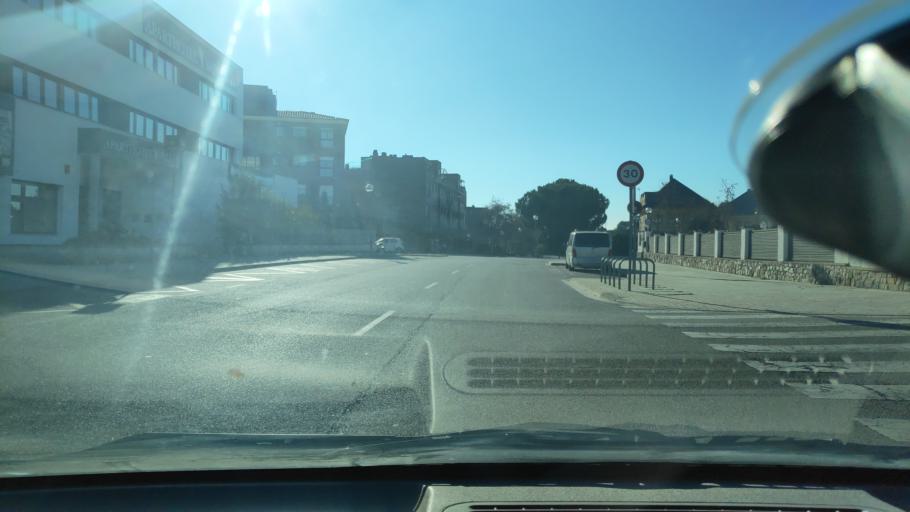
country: ES
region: Catalonia
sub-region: Provincia de Barcelona
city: Sant Quirze del Valles
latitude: 41.5564
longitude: 2.0766
